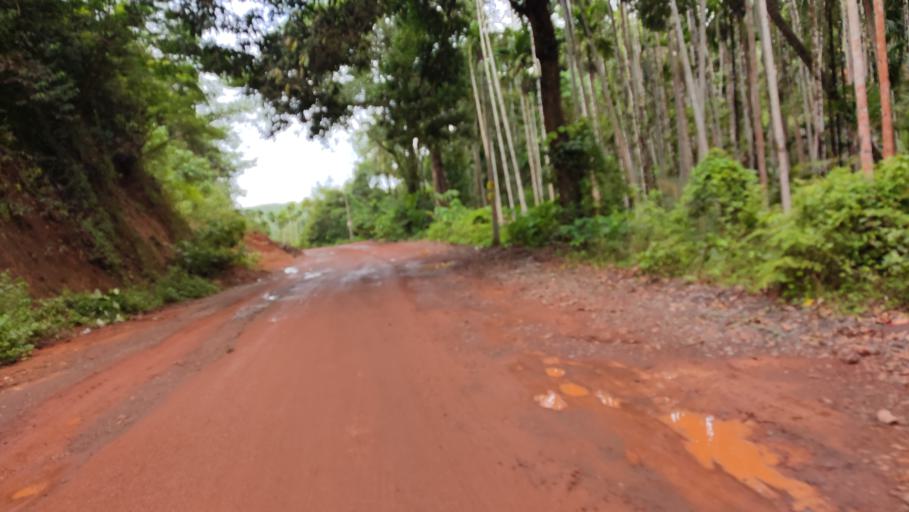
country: IN
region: Kerala
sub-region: Kasaragod District
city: Kasaragod
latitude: 12.5274
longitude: 75.0709
